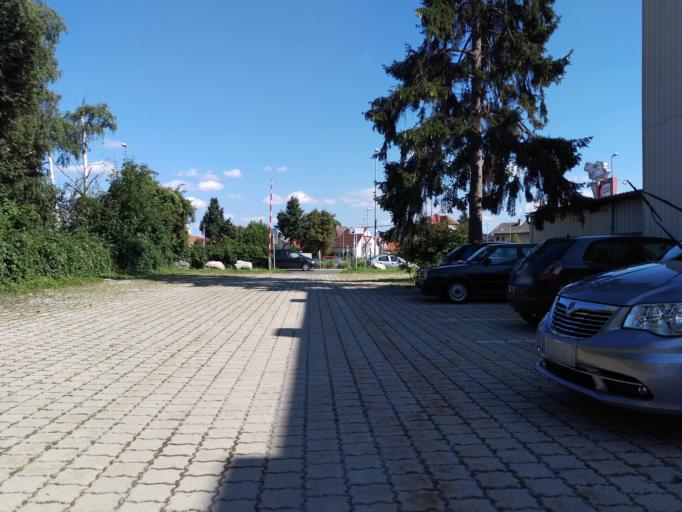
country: AT
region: Styria
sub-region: Graz Stadt
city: Wetzelsdorf
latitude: 47.0601
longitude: 15.4200
